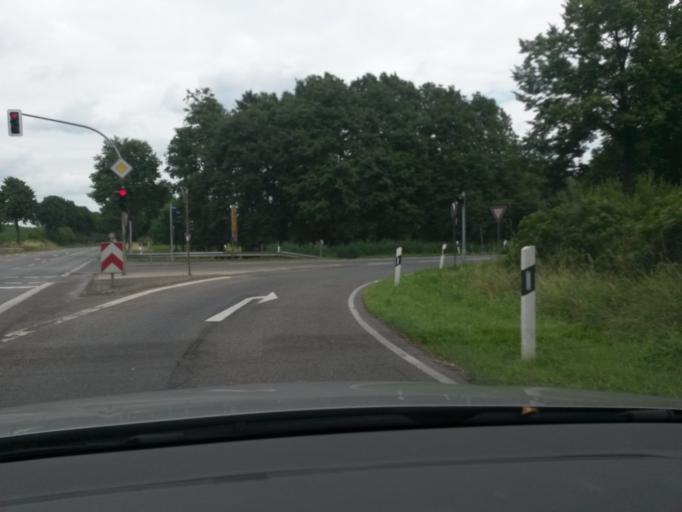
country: DE
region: North Rhine-Westphalia
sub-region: Regierungsbezirk Dusseldorf
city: Nettetal
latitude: 51.2874
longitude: 6.2800
